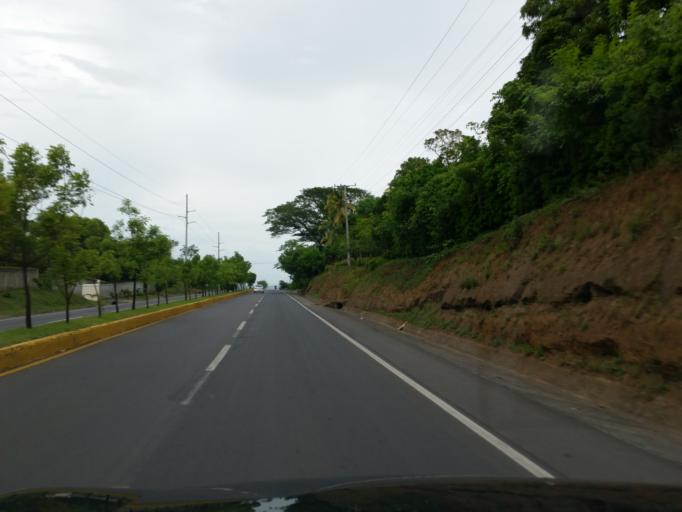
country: NI
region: Masaya
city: Masaya
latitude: 11.9758
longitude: -86.0603
